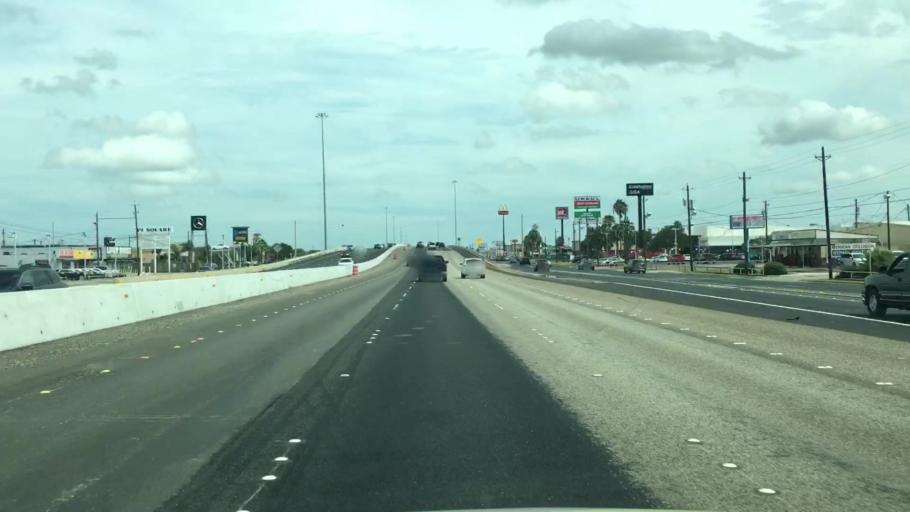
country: US
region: Texas
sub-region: Nueces County
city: Corpus Christi
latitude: 27.7302
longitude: -97.4164
